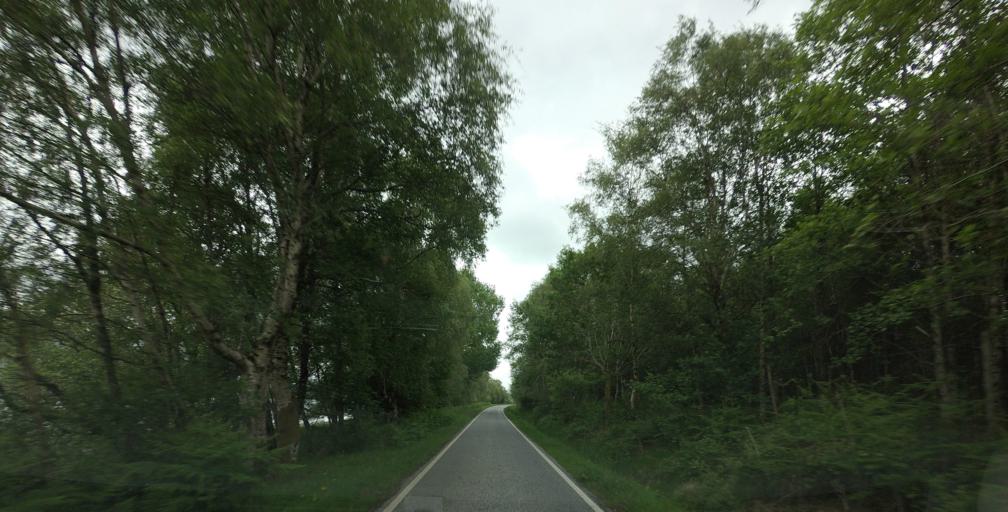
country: GB
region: Scotland
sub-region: Highland
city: Fort William
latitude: 56.8424
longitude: -5.2529
